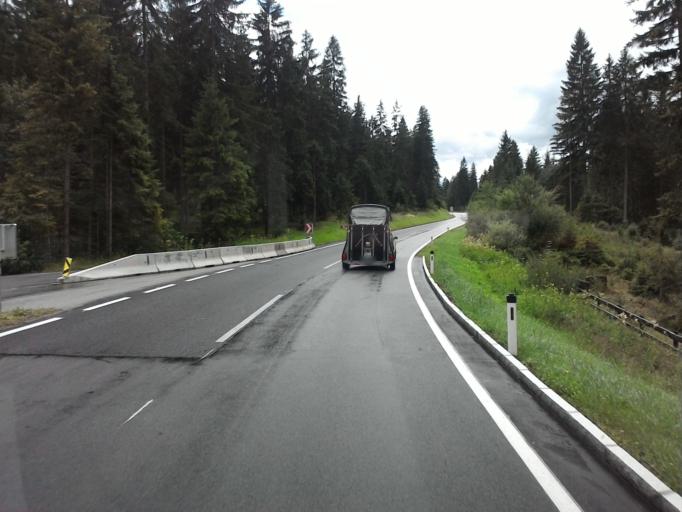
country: AT
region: Tyrol
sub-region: Politischer Bezirk Innsbruck Land
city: Seefeld in Tirol
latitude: 47.3577
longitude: 11.2262
